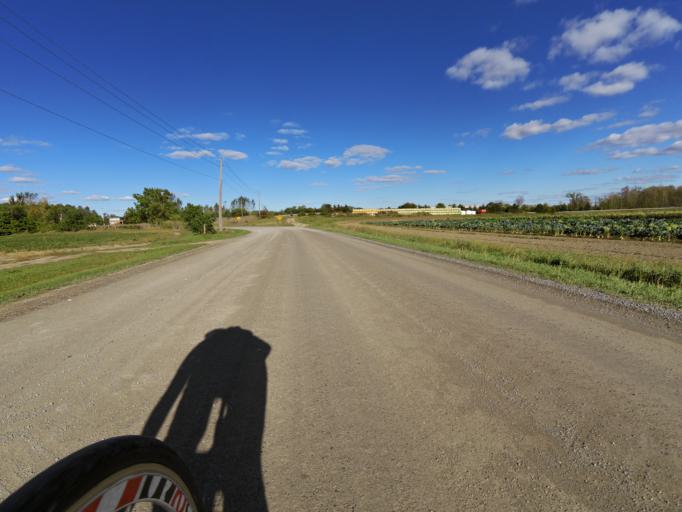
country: CA
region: Ontario
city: Bells Corners
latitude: 45.1256
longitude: -75.6783
